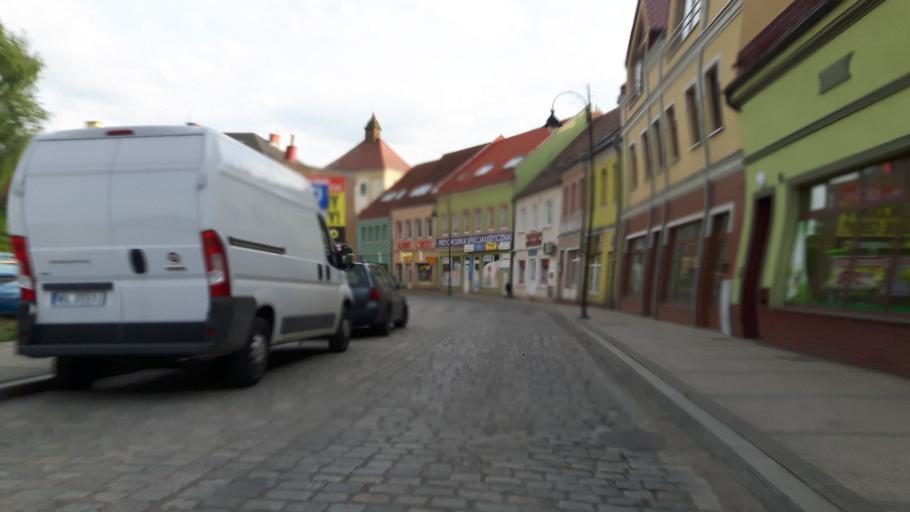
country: PL
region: West Pomeranian Voivodeship
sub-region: Powiat gryficki
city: Gryfice
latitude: 53.9126
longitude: 15.1973
